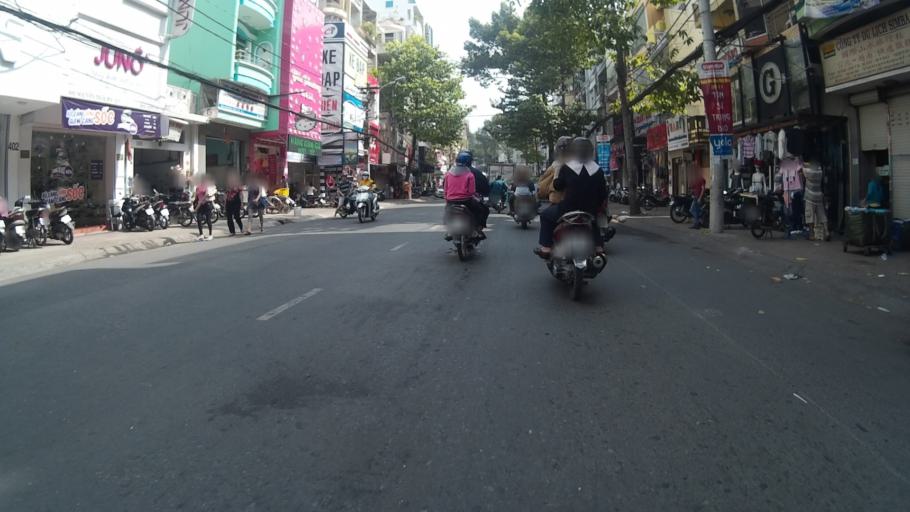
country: VN
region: Ho Chi Minh City
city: Quan Nam
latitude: 10.7553
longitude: 106.6727
